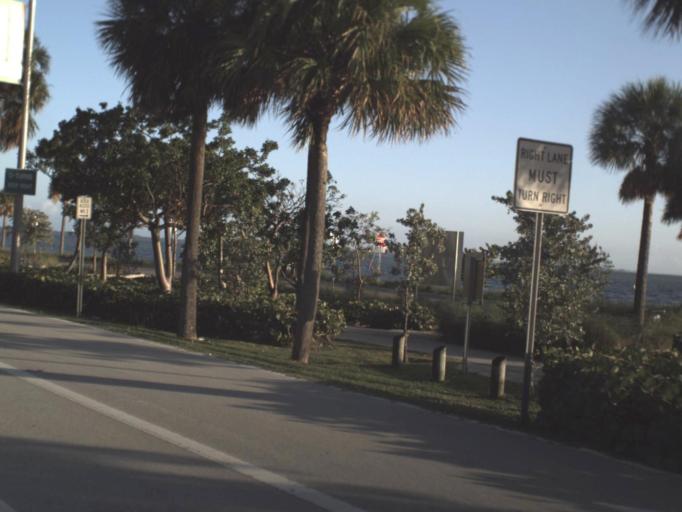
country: US
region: Florida
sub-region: Miami-Dade County
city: Miami
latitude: 25.7463
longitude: -80.1991
